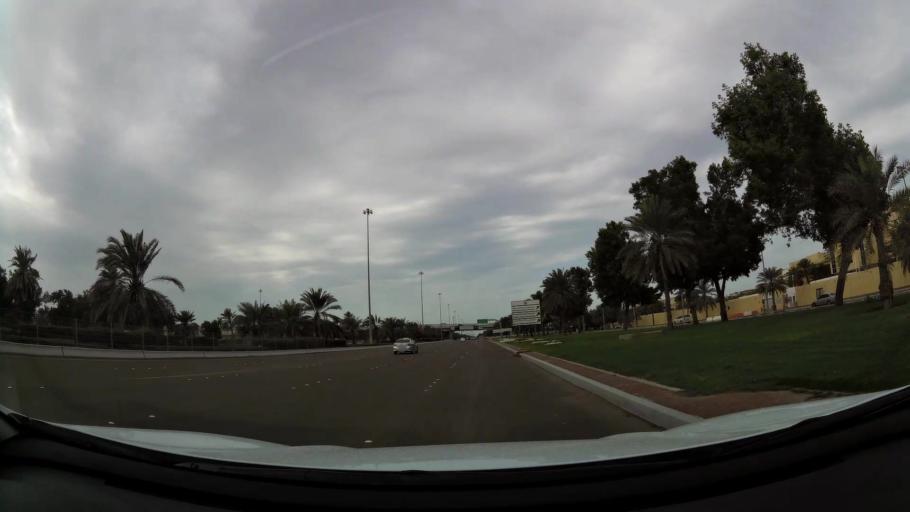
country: AE
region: Abu Dhabi
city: Abu Dhabi
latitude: 24.4220
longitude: 54.4199
